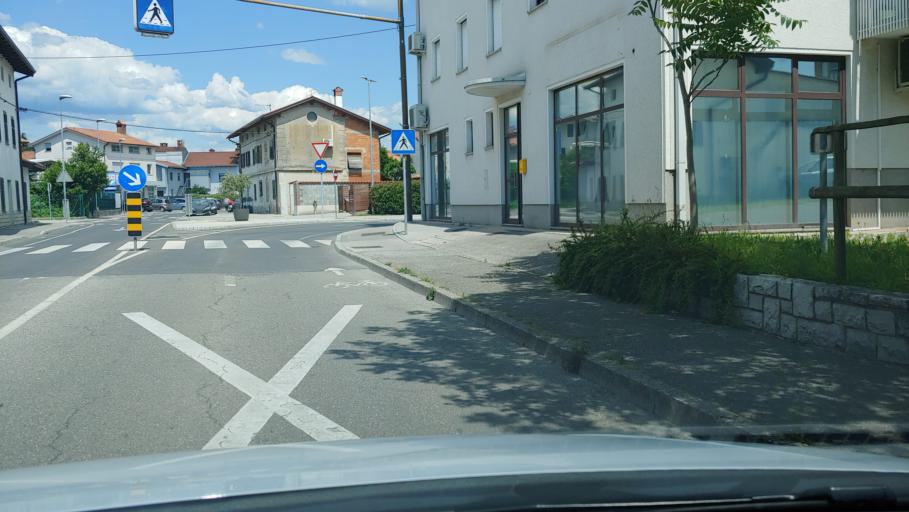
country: SI
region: Sempeter-Vrtojba
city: Sempeter pri Gorici
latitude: 45.9280
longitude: 13.6402
